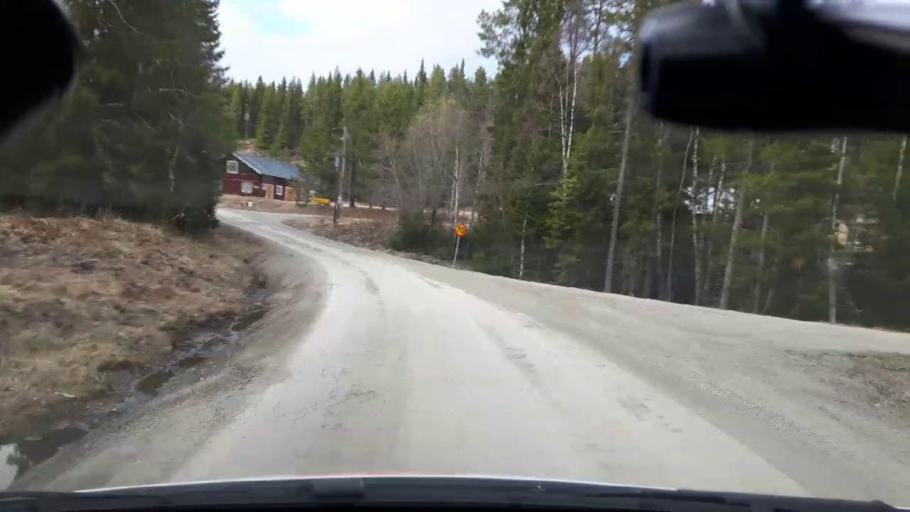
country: SE
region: Jaemtland
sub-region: OEstersunds Kommun
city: Brunflo
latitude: 62.9450
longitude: 14.6670
